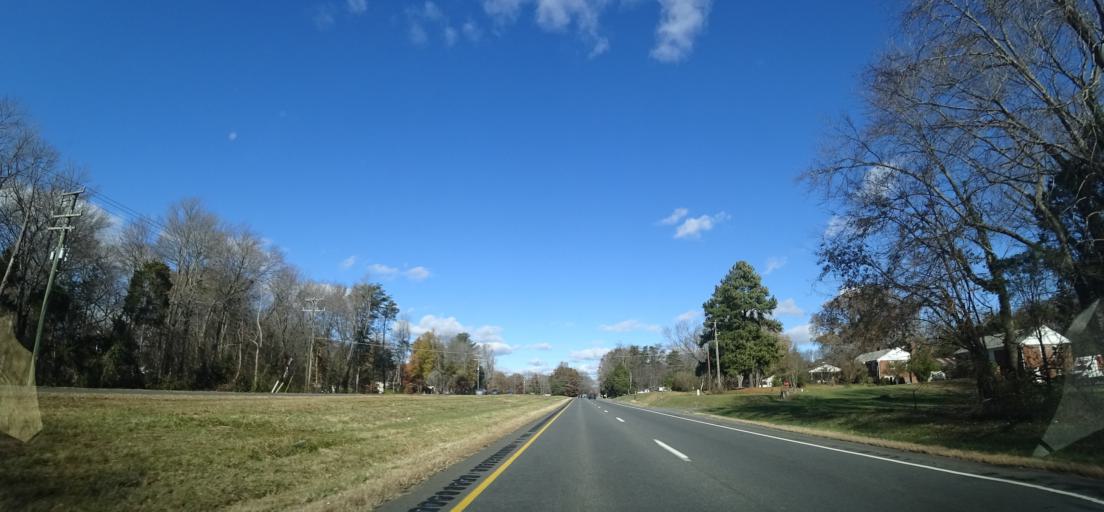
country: US
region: Virginia
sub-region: Fauquier County
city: Bealeton
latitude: 38.5824
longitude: -77.8020
